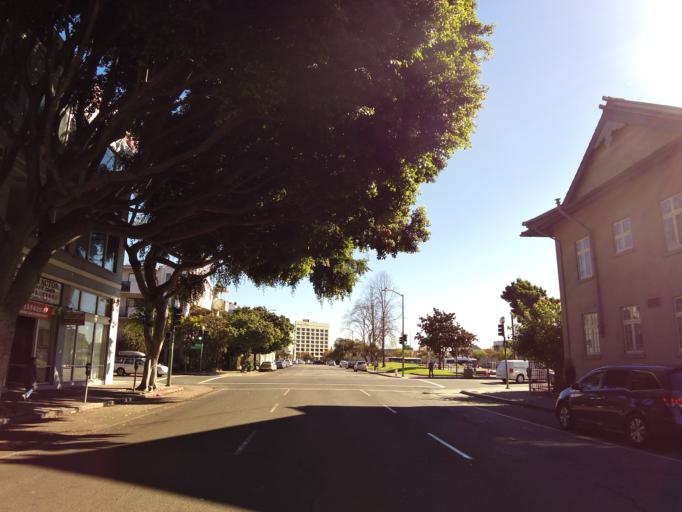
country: US
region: California
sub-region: Alameda County
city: Oakland
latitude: 37.7987
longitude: -122.2679
